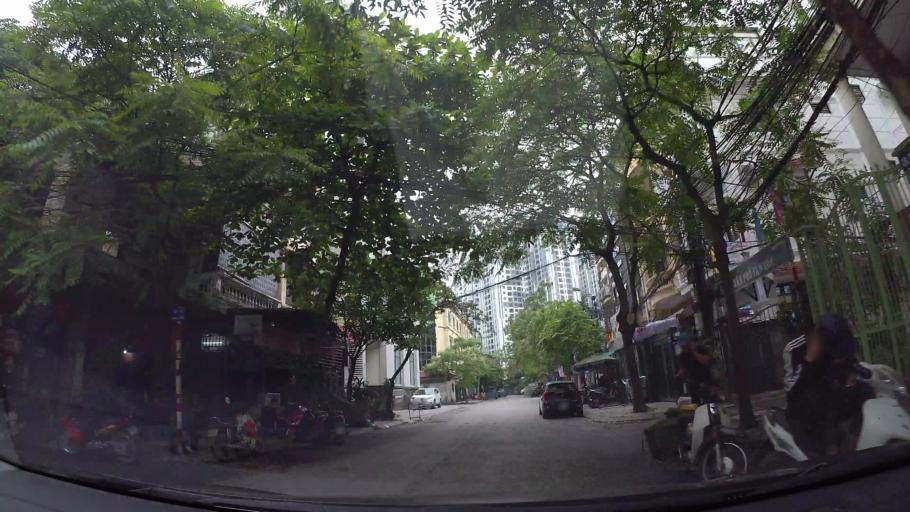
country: VN
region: Ha Noi
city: Hai BaTrung
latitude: 21.0015
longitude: 105.8668
